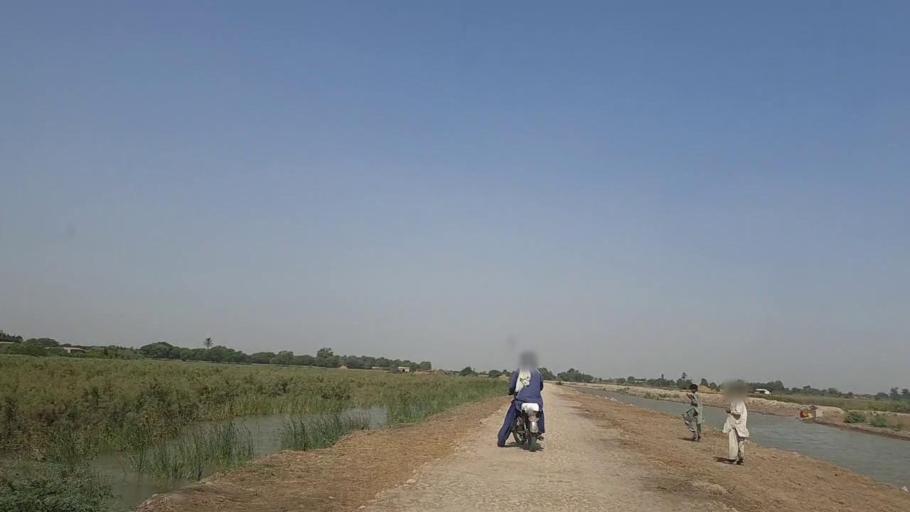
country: PK
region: Sindh
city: Daro Mehar
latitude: 24.7603
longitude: 68.1359
